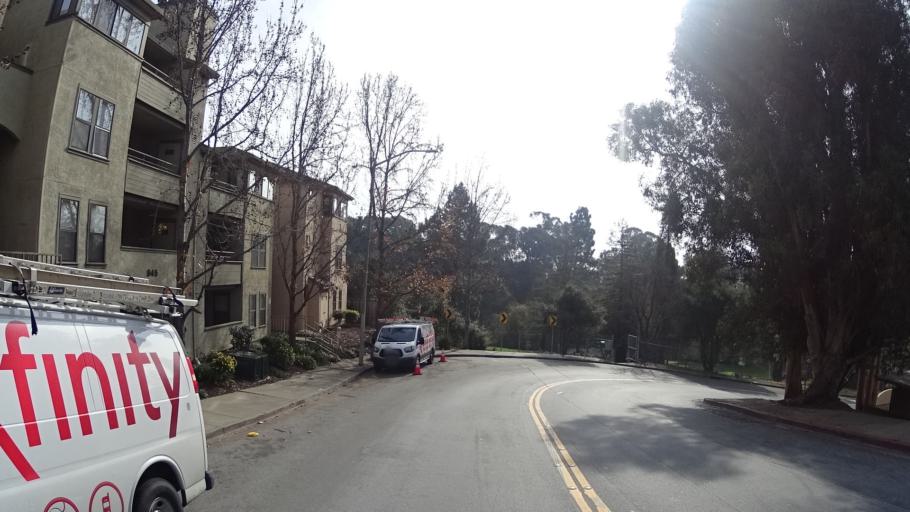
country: US
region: California
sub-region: Alameda County
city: Hayward
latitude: 37.6671
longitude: -122.0768
